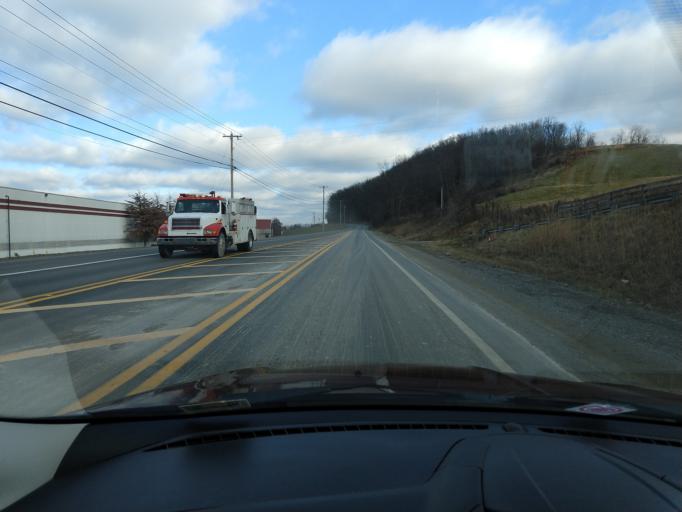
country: US
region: West Virginia
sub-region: Randolph County
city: Elkins
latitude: 38.8157
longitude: -79.8775
